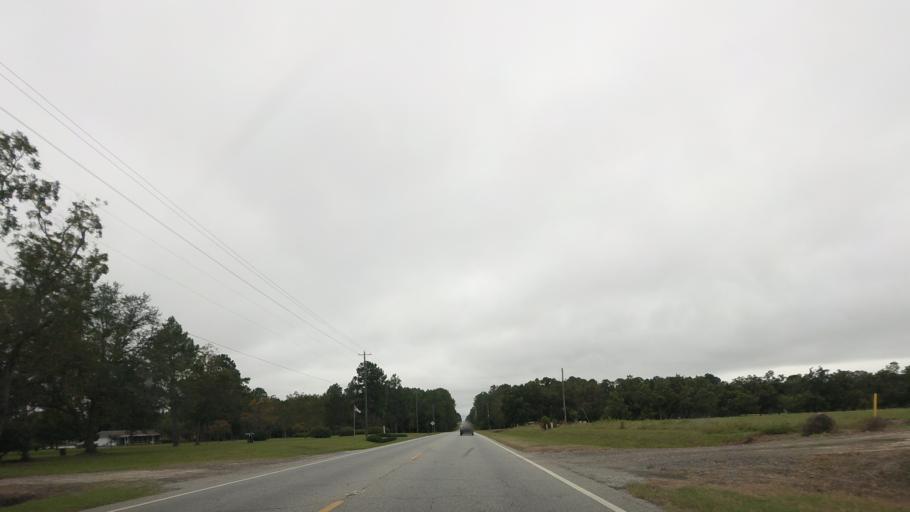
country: US
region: Georgia
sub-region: Berrien County
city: Ray City
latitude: 31.0111
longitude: -83.1982
